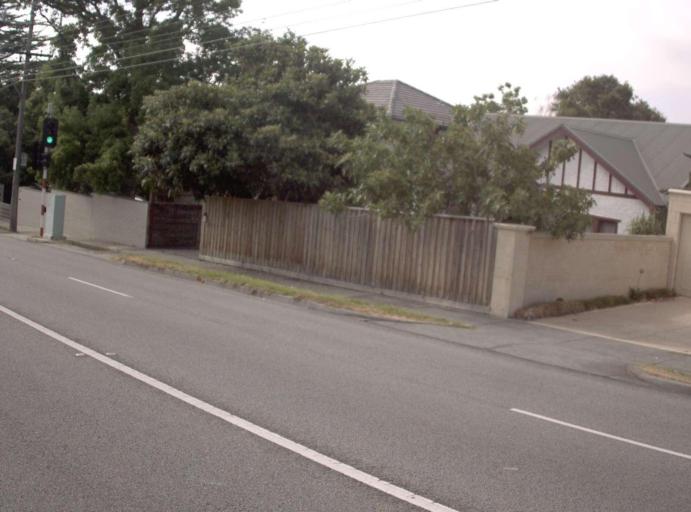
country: AU
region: Victoria
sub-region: Boroondara
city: Camberwell
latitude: -37.8466
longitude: 145.0622
